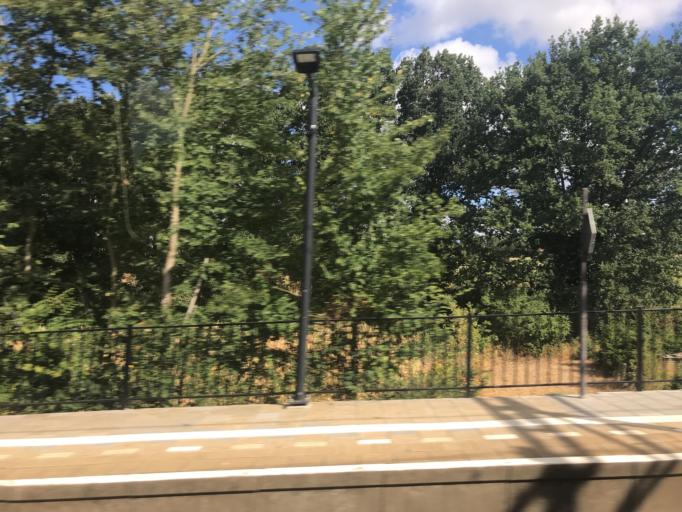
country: NL
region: Overijssel
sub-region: Gemeente Hof van Twente
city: Markelo
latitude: 52.2835
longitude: 6.4188
